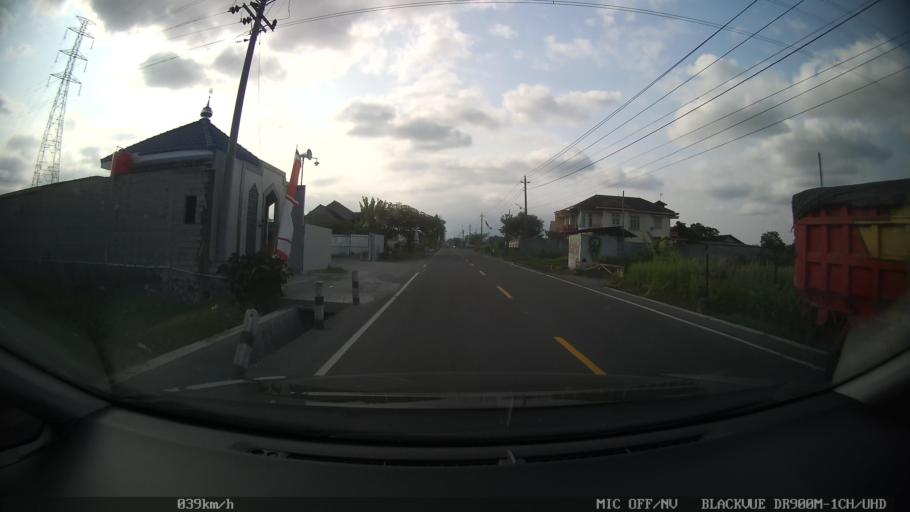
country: ID
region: Central Java
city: Candi Prambanan
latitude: -7.7138
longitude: 110.4710
